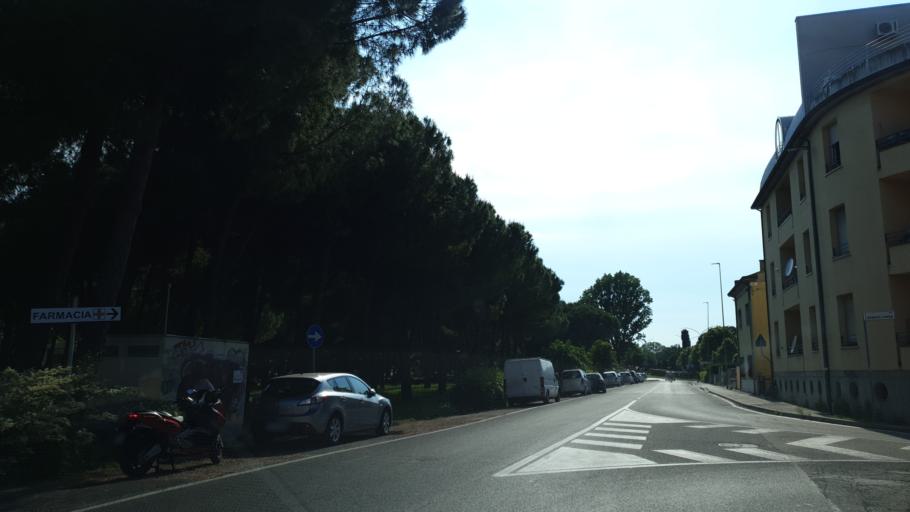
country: IT
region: Emilia-Romagna
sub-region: Provincia di Ravenna
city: Ravenna
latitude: 44.4244
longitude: 12.2115
